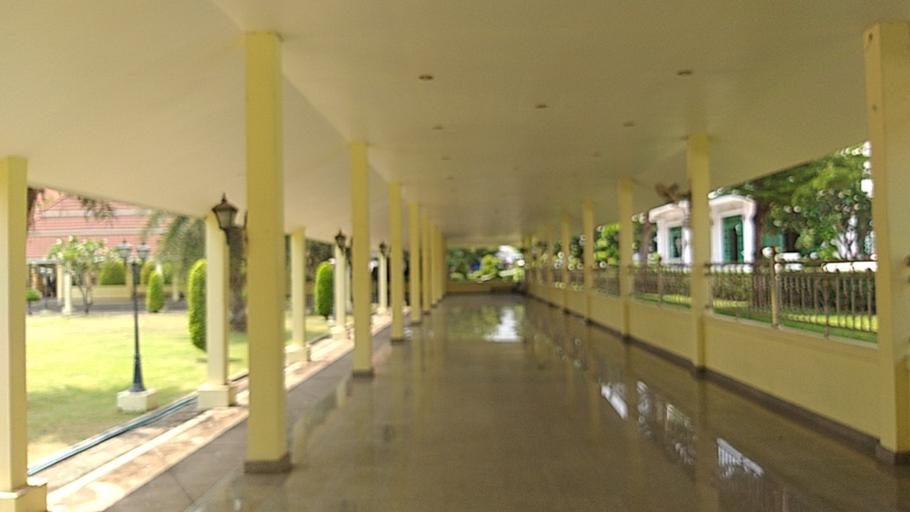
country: TH
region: Pathum Thani
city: Sam Khok
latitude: 14.1143
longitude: 100.5411
